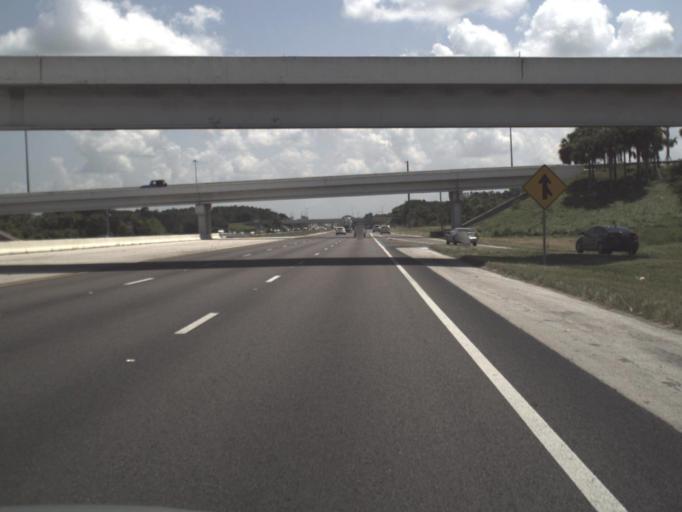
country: US
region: Florida
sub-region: Hillsborough County
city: Mango
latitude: 28.0020
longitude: -82.3262
